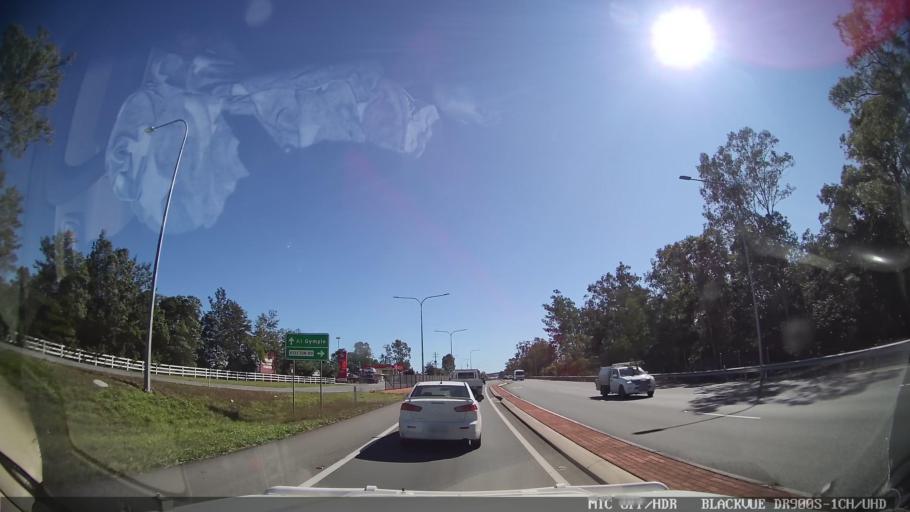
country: AU
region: Queensland
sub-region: Gympie Regional Council
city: Monkland
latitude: -26.2396
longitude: 152.6999
